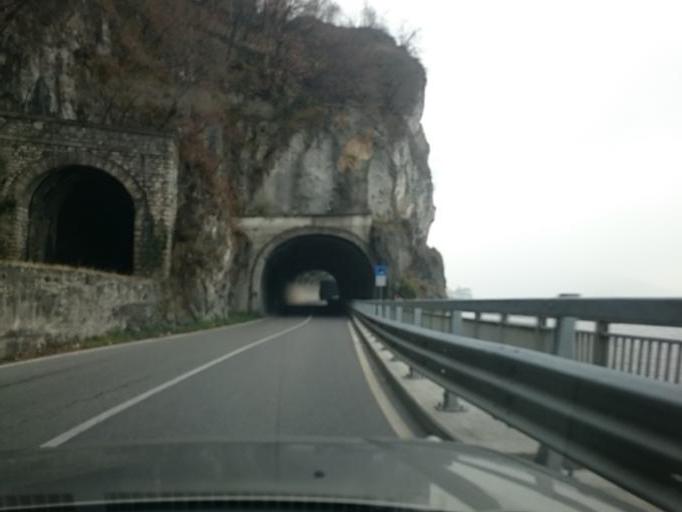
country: IT
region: Lombardy
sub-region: Provincia di Brescia
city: Marone
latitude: 45.7442
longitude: 10.0902
